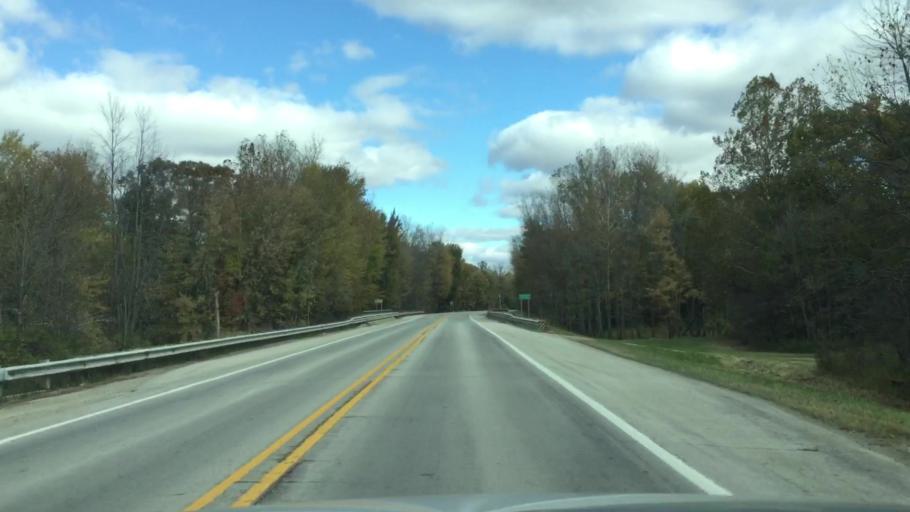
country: US
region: Michigan
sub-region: Lapeer County
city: Barnes Lake-Millers Lake
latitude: 43.2234
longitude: -83.3017
